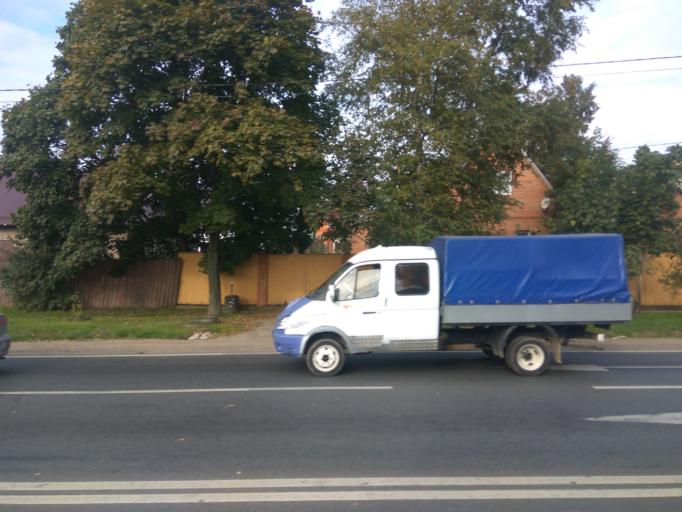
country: RU
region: Moskovskaya
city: Balashikha
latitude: 55.8379
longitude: 37.9468
